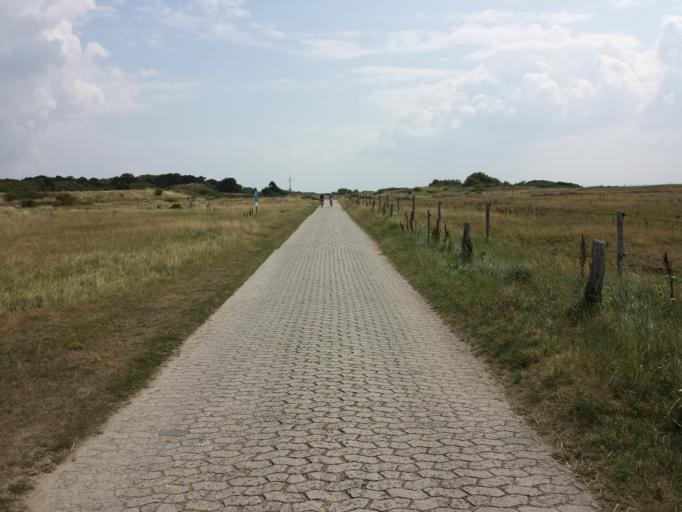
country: DE
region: Lower Saxony
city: Spiekeroog
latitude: 53.7692
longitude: 7.7068
